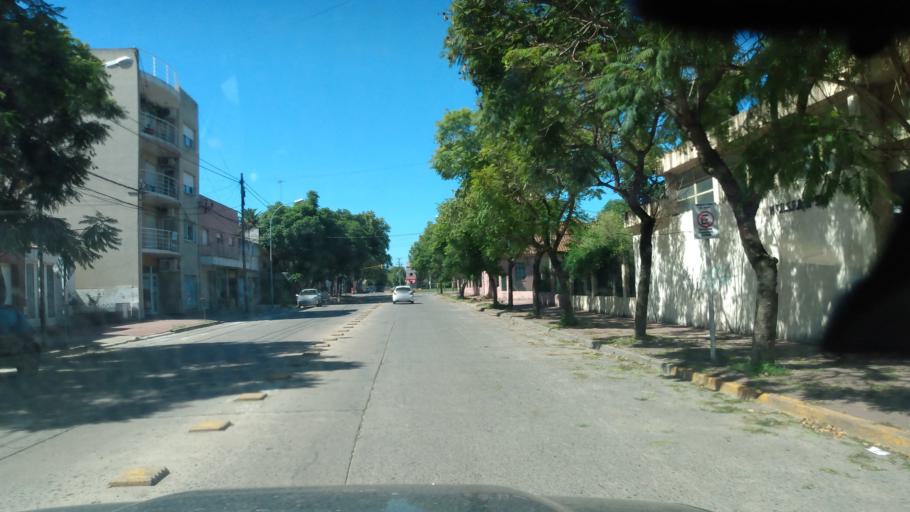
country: AR
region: Buenos Aires
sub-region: Partido de Lujan
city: Lujan
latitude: -34.5712
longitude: -59.1145
